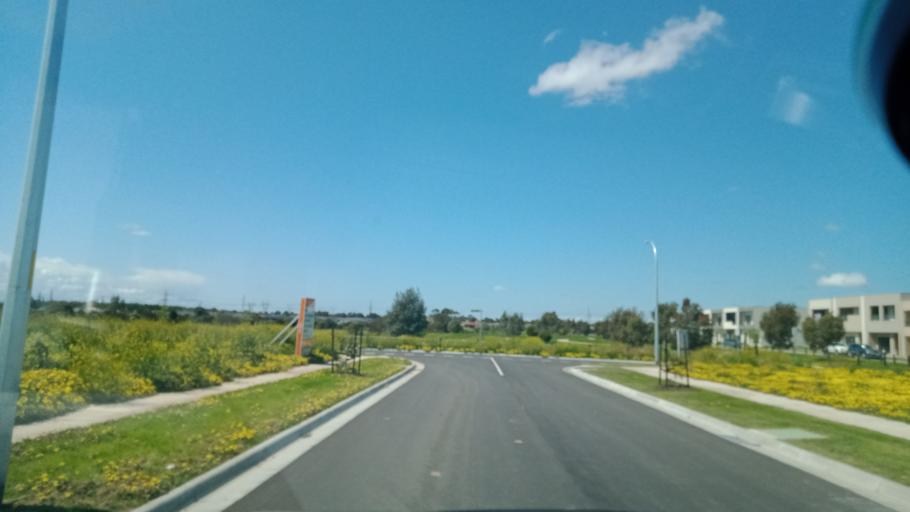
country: AU
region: Victoria
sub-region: Casey
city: Cranbourne West
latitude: -38.0899
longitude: 145.2523
